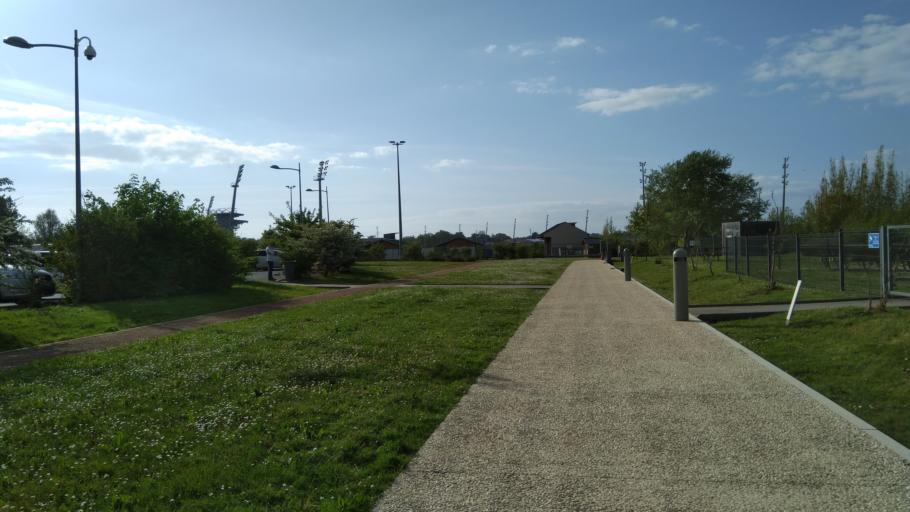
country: FR
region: Pays de la Loire
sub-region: Departement de la Loire-Atlantique
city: Pornichet
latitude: 47.2590
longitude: -2.3260
